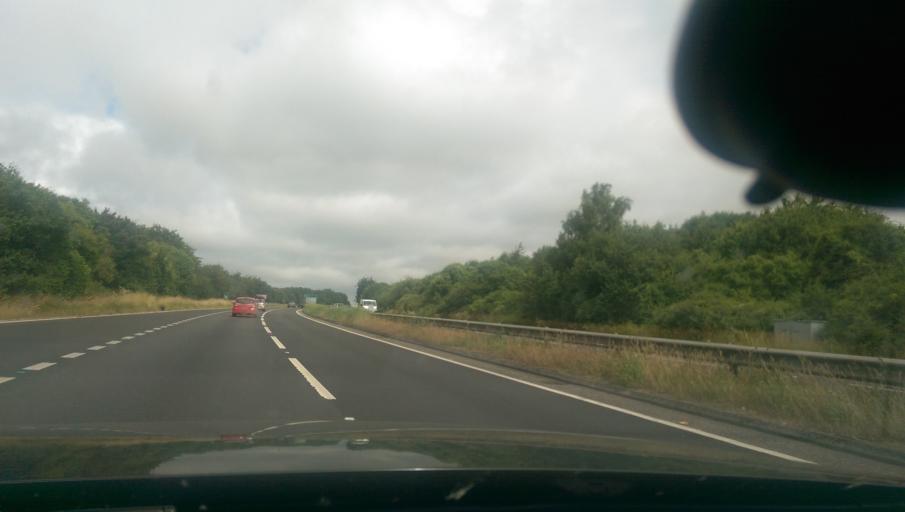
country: GB
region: England
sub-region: Hampshire
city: Andover
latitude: 51.2027
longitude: -1.5103
